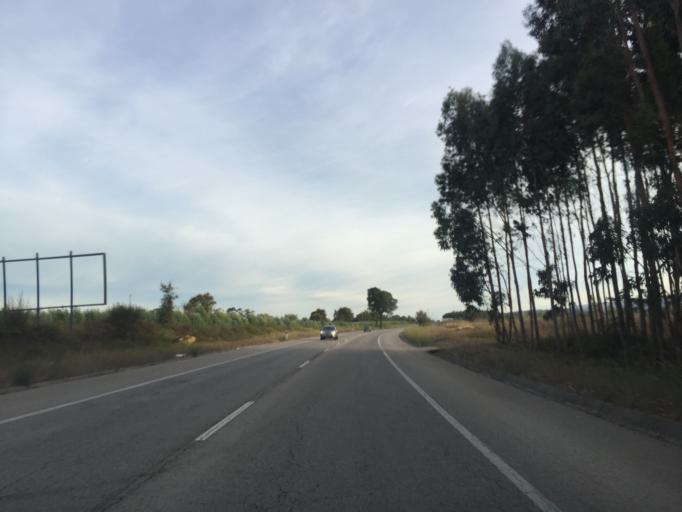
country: PT
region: Leiria
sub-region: Alcobaca
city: Benedita
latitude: 39.4181
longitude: -8.9632
